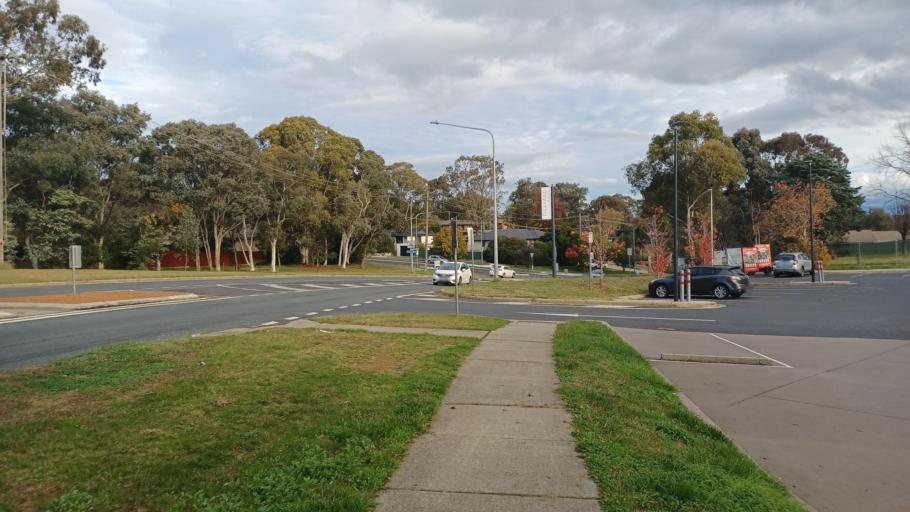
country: AU
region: Australian Capital Territory
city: Belconnen
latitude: -35.1982
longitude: 149.0445
